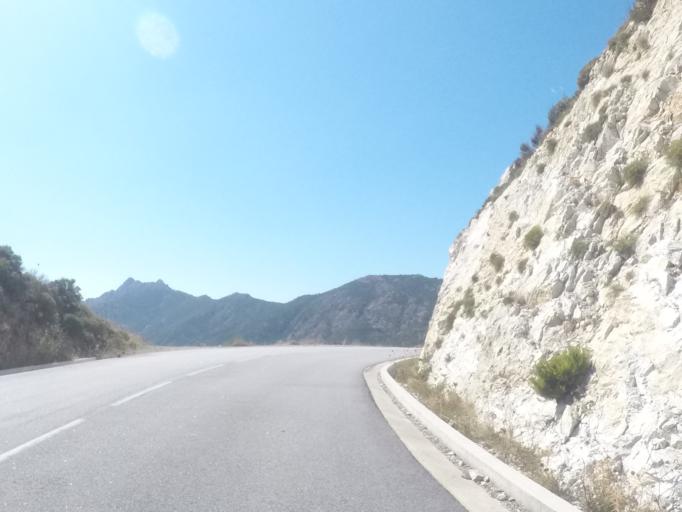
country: FR
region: Corsica
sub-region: Departement de la Haute-Corse
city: Calvi
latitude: 42.4759
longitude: 8.7560
